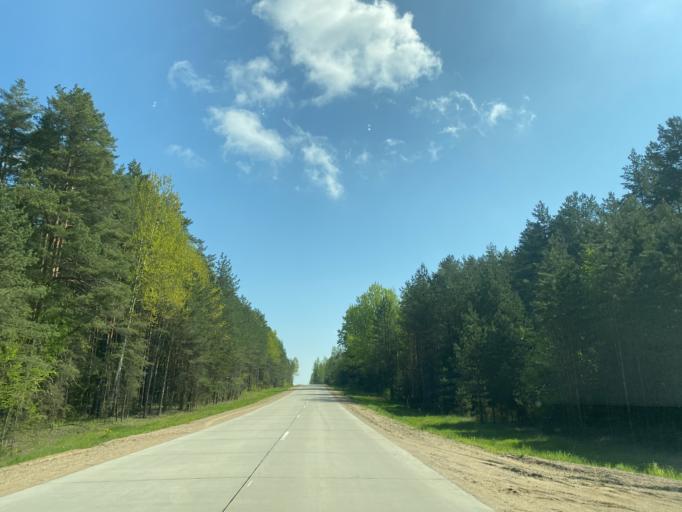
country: BY
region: Minsk
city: Horad Barysaw
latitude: 54.1617
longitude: 28.4931
